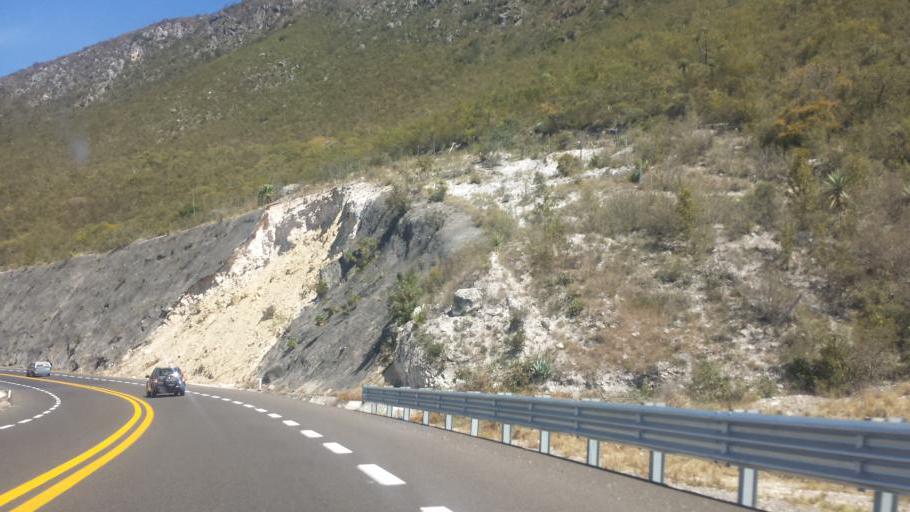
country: MX
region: Puebla
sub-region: San Jose Miahuatlan
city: San Pedro Tetitlan
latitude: 18.0444
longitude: -97.3505
